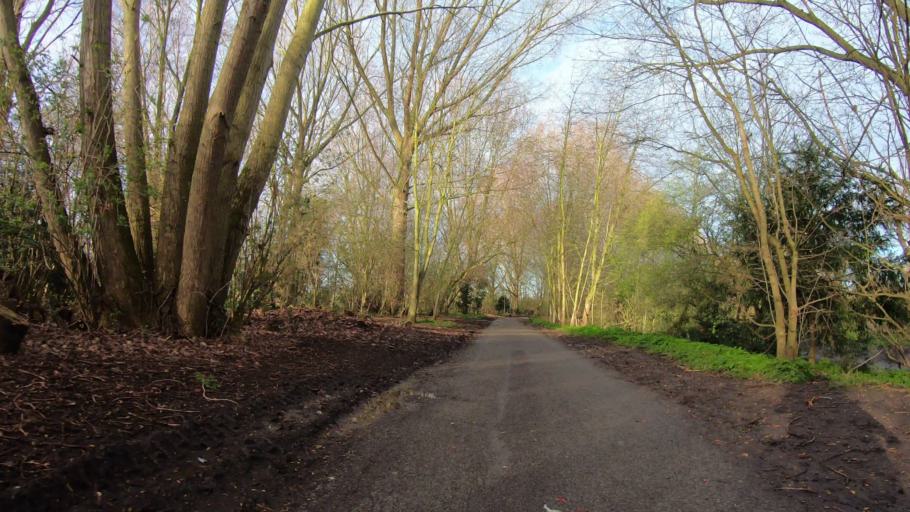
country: GB
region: England
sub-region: Greater London
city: Hackney
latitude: 51.5524
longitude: -0.0217
